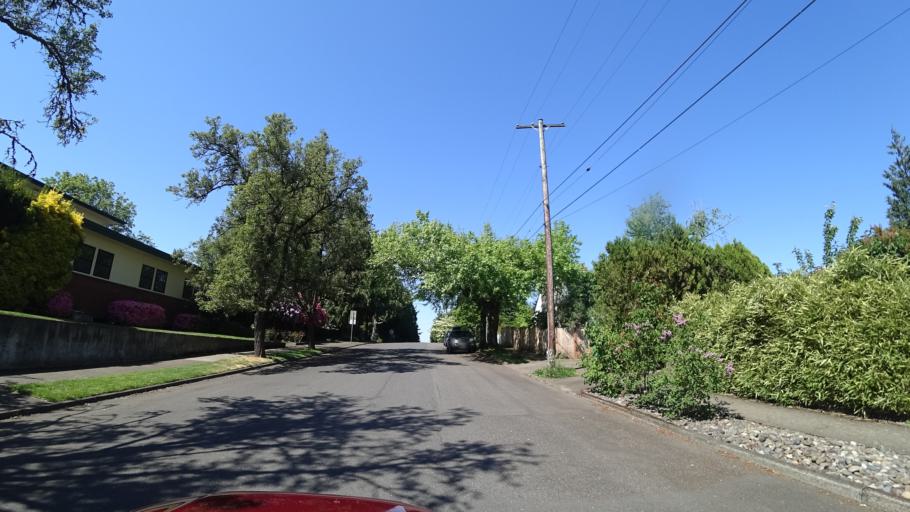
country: US
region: Oregon
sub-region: Multnomah County
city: Lents
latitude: 45.4985
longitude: -122.6164
